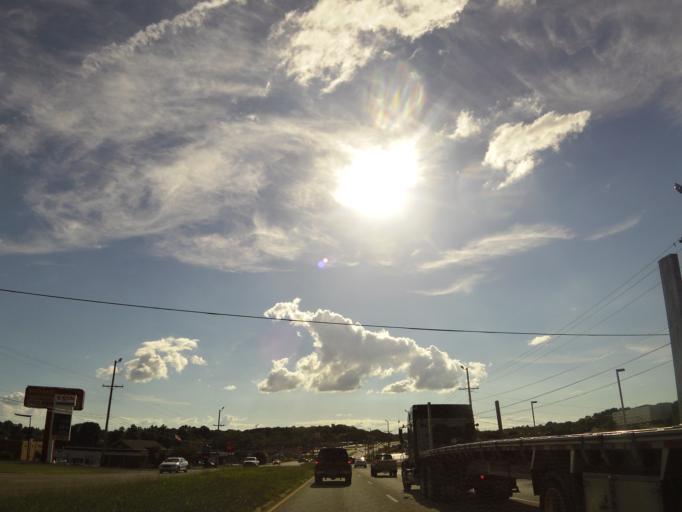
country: US
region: Tennessee
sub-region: Greene County
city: Tusculum
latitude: 36.1774
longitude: -82.7924
